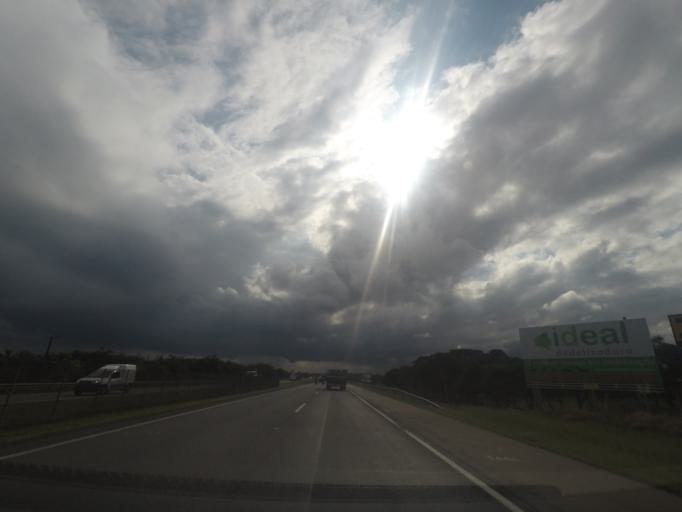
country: BR
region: Parana
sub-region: Sao Jose Dos Pinhais
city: Sao Jose dos Pinhais
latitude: -25.5006
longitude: -49.1522
